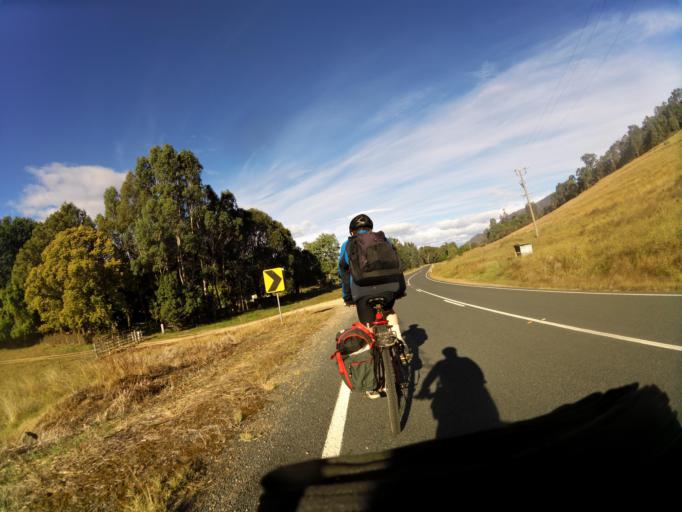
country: AU
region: New South Wales
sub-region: Greater Hume Shire
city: Holbrook
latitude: -35.9725
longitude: 147.8057
